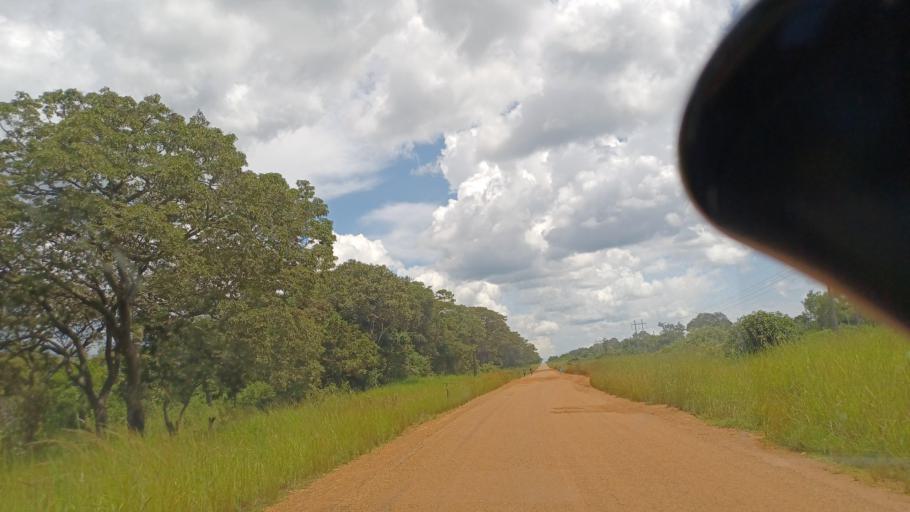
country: ZM
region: North-Western
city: Solwezi
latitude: -12.6975
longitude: 26.0388
